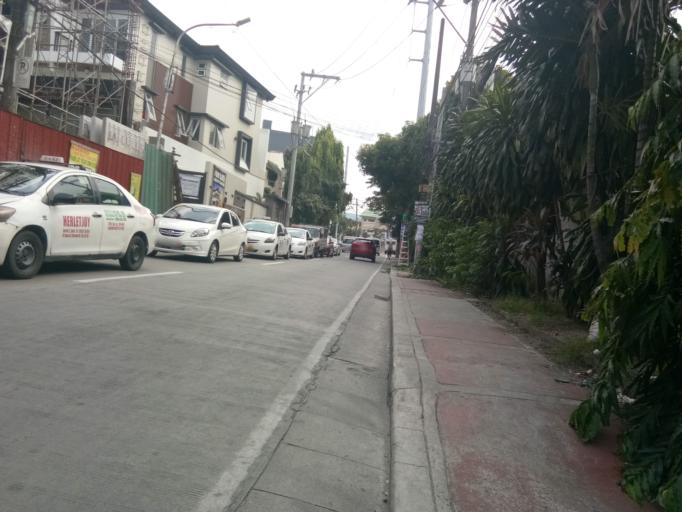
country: PH
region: Metro Manila
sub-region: San Juan
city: San Juan
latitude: 14.6149
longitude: 121.0470
